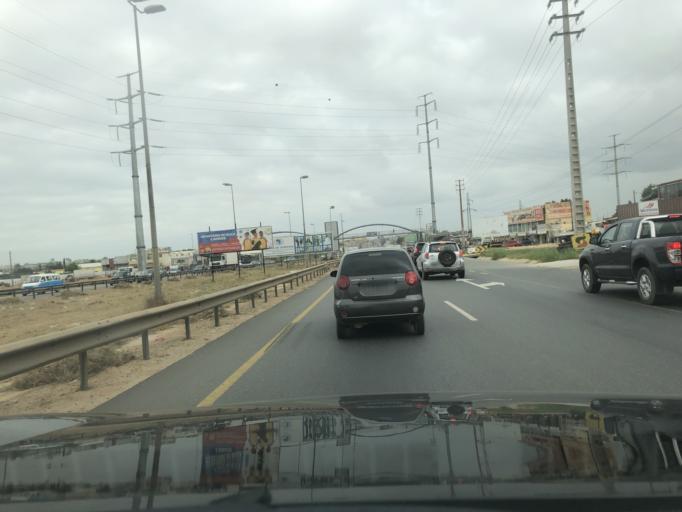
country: AO
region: Luanda
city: Luanda
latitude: -8.9746
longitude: 13.2126
